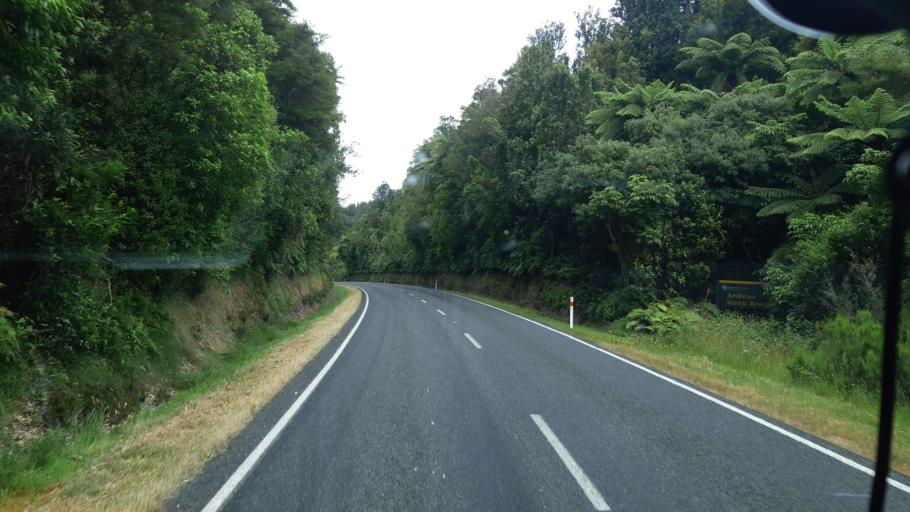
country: NZ
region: Waikato
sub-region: South Waikato District
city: Tokoroa
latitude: -38.2472
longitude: 175.6431
